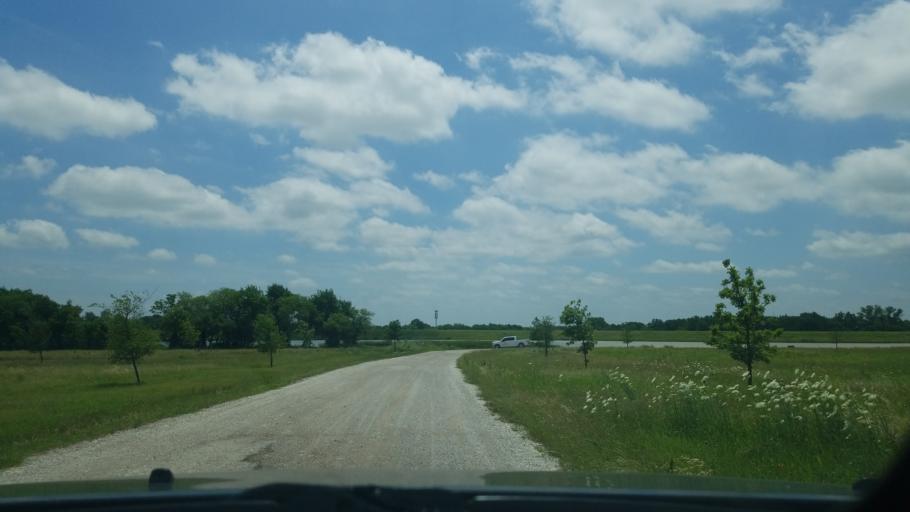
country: US
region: Texas
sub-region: Denton County
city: Denton
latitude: 33.2363
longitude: -97.1592
